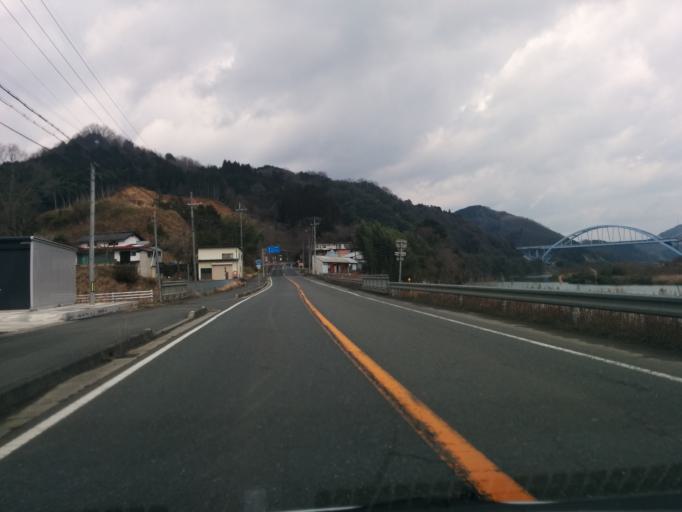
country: JP
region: Kyoto
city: Miyazu
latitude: 35.4187
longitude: 135.2035
